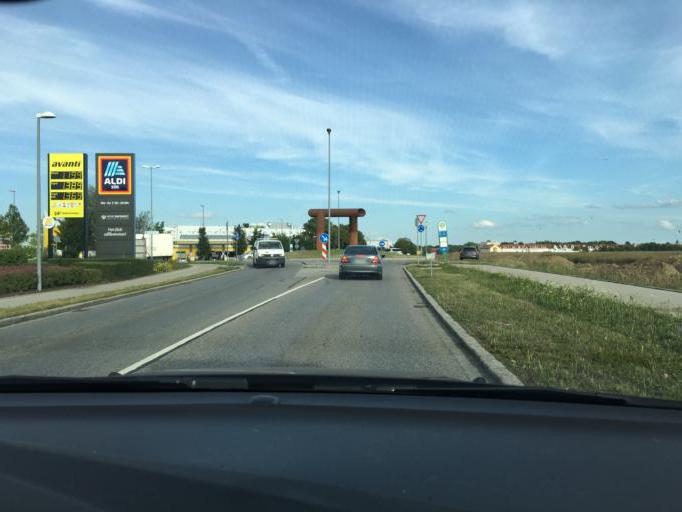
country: DE
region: Bavaria
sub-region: Upper Bavaria
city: Stammham
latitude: 48.3067
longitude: 11.8843
